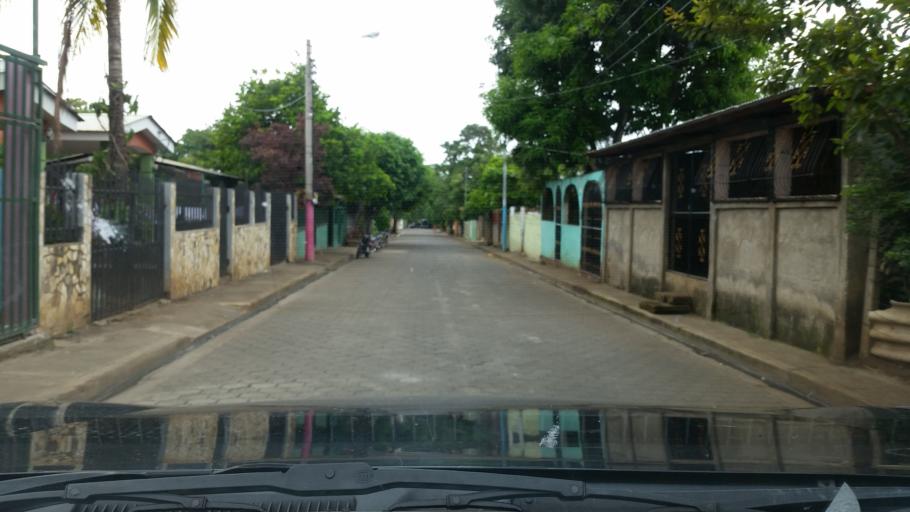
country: NI
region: Masaya
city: Ticuantepe
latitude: 12.0242
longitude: -86.2095
